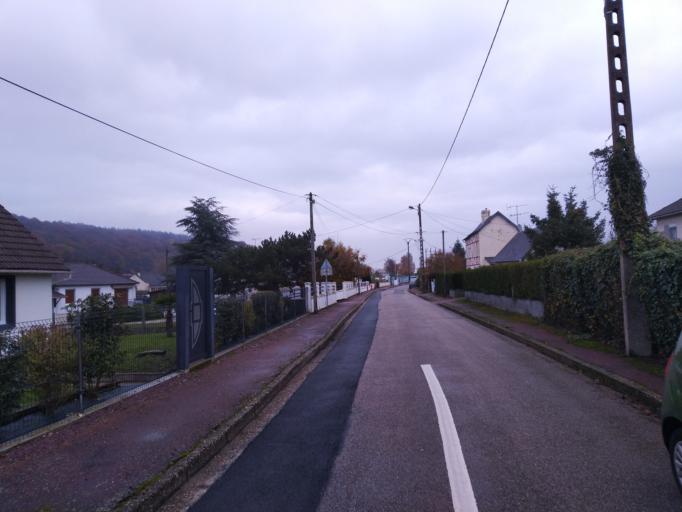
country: FR
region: Haute-Normandie
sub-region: Departement de la Seine-Maritime
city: Yainville
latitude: 49.4586
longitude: 0.8340
